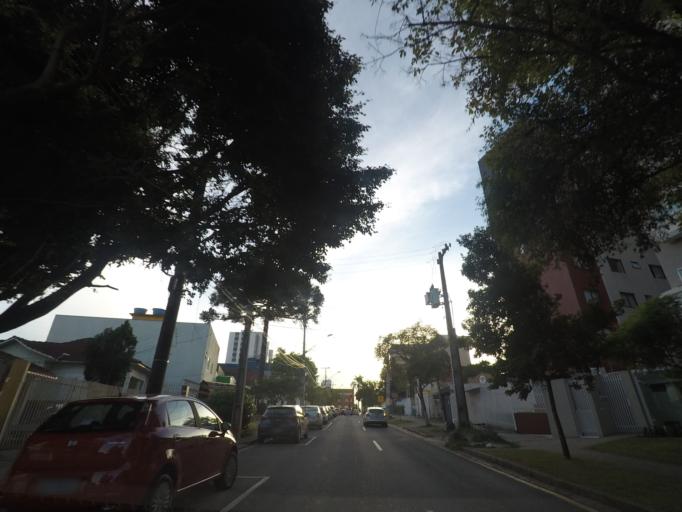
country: BR
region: Parana
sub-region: Curitiba
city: Curitiba
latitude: -25.4124
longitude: -49.2625
